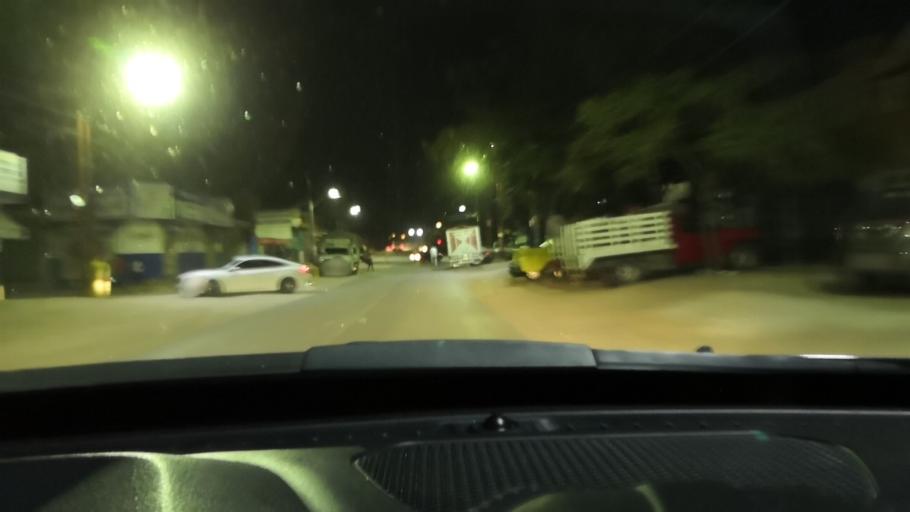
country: MX
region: Guanajuato
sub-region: Leon
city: Medina
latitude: 21.1369
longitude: -101.6454
